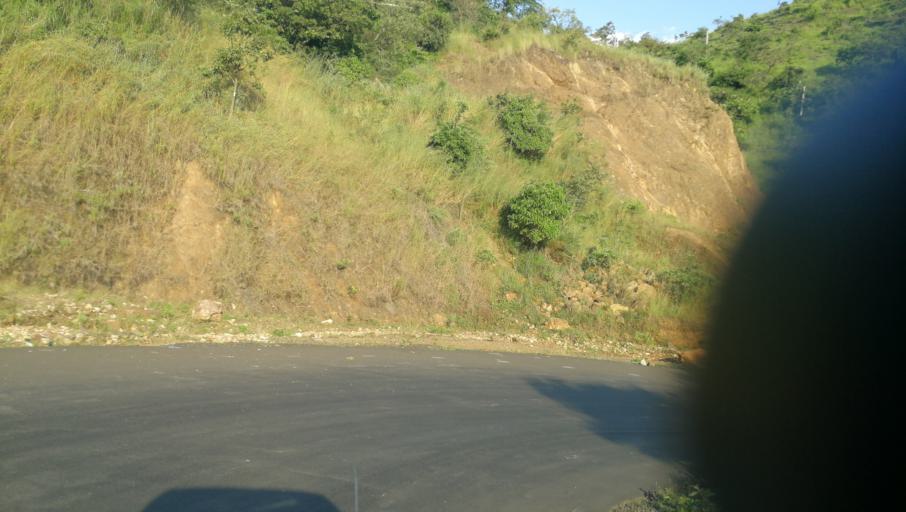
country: ET
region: Southern Nations, Nationalities, and People's Region
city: Areka
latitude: 6.8251
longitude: 37.3042
